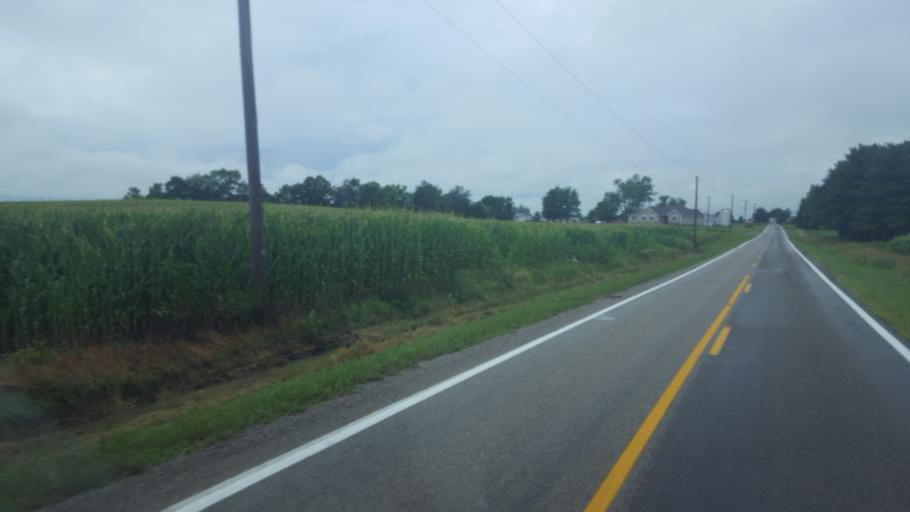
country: US
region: Ohio
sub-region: Union County
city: Richwood
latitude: 40.5016
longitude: -83.3310
